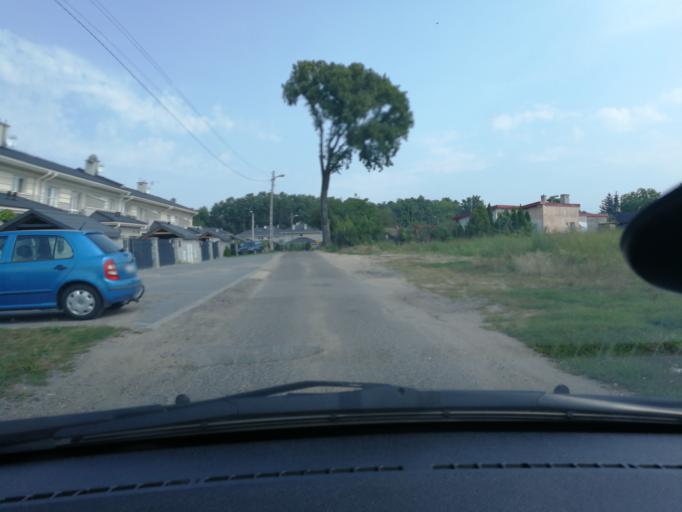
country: PL
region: Lodz Voivodeship
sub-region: Skierniewice
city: Skierniewice
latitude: 51.9730
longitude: 20.1241
